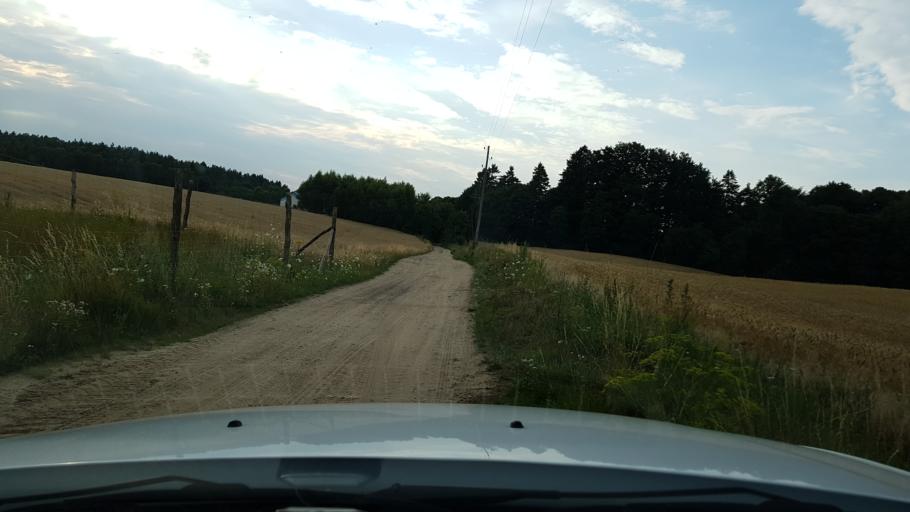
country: PL
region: West Pomeranian Voivodeship
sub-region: Powiat swidwinski
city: Polczyn-Zdroj
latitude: 53.7994
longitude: 16.0782
